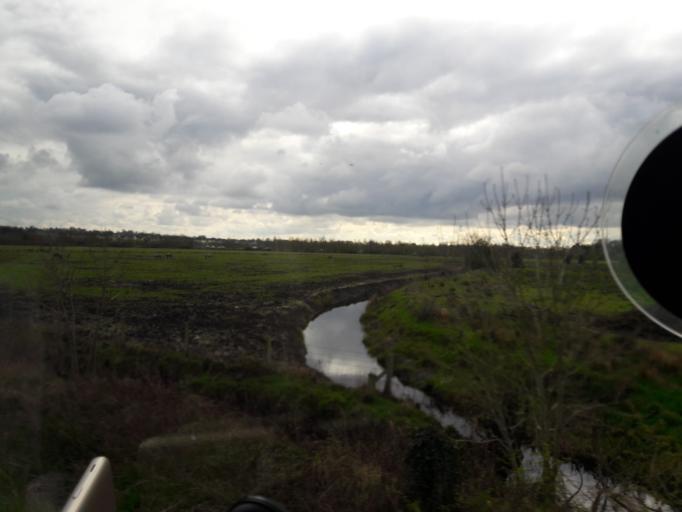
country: IE
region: Leinster
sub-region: An Longfort
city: Longford
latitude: 53.7268
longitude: -7.8169
